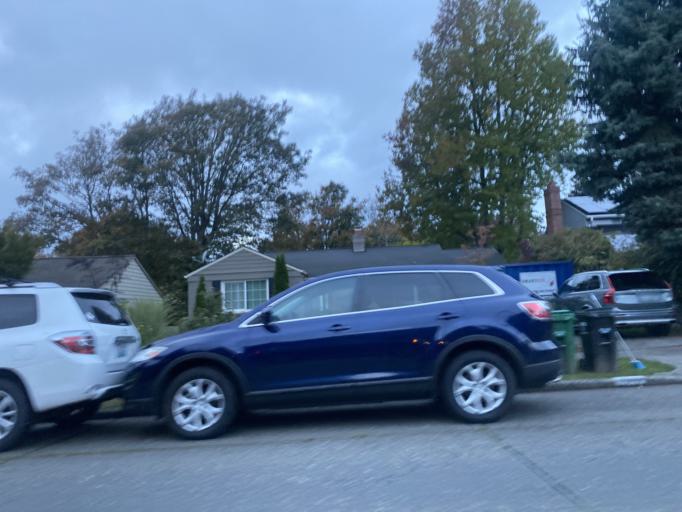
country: US
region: Washington
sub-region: King County
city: Seattle
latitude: 47.6363
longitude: -122.3979
